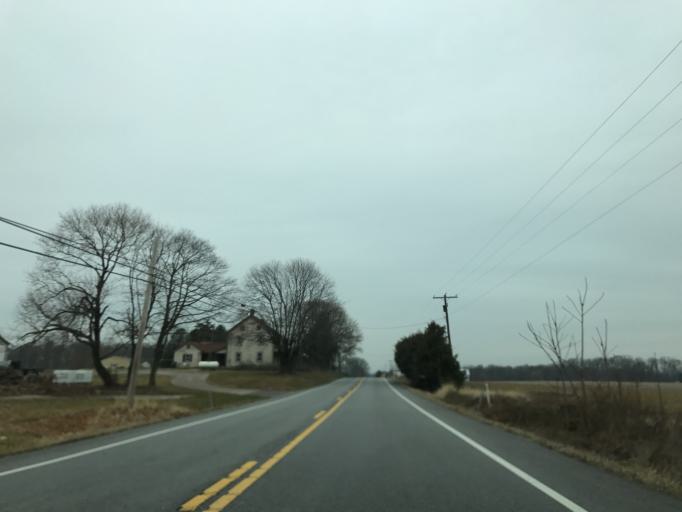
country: US
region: Maryland
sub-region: Carroll County
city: Taneytown
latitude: 39.6765
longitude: -77.2201
